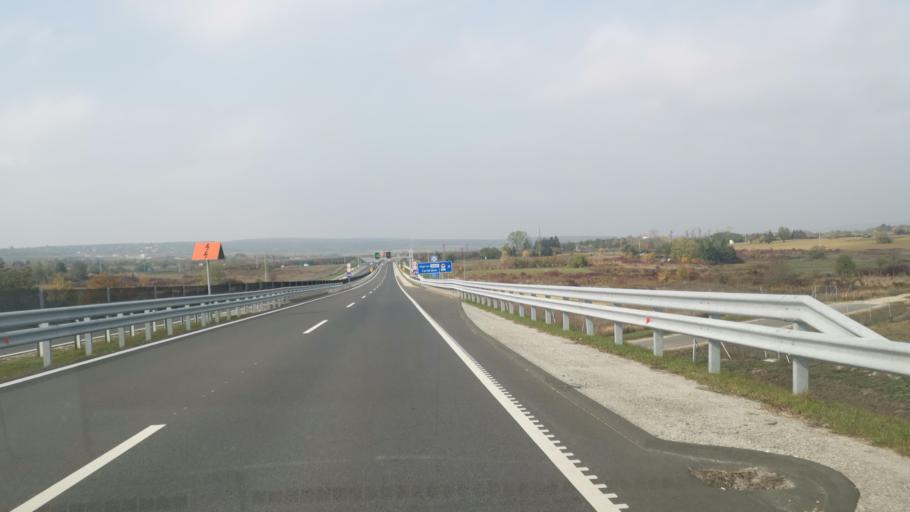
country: HU
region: Gyor-Moson-Sopron
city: Sopron
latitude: 47.7012
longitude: 16.6131
